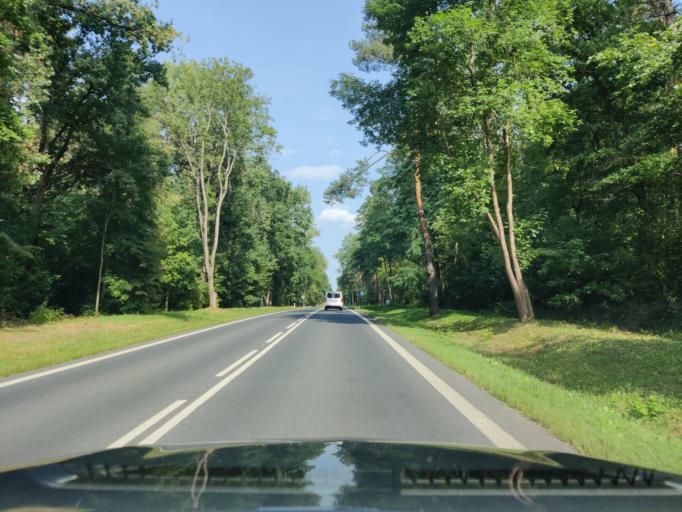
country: PL
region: Masovian Voivodeship
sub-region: Powiat makowski
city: Rzewnie
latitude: 52.8519
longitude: 21.2908
